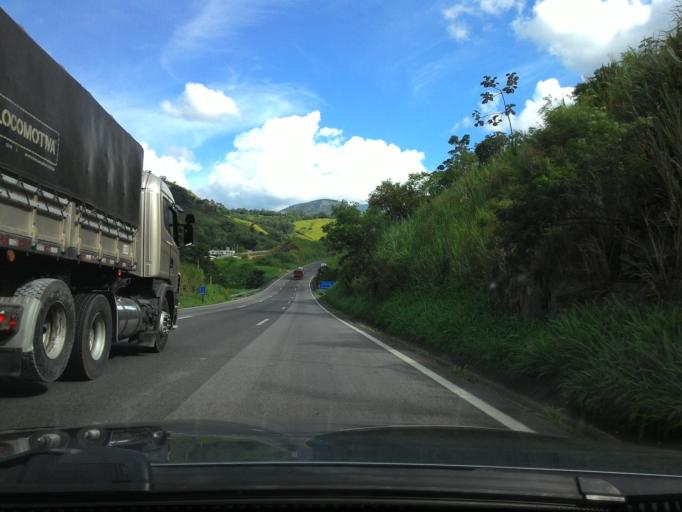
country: BR
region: Sao Paulo
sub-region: Cajati
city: Cajati
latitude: -24.7976
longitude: -48.2143
